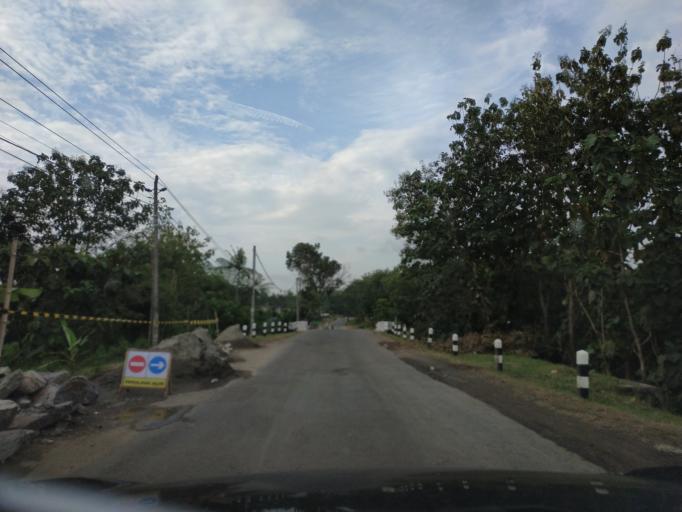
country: ID
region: Central Java
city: Medang
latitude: -6.9064
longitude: 111.4412
